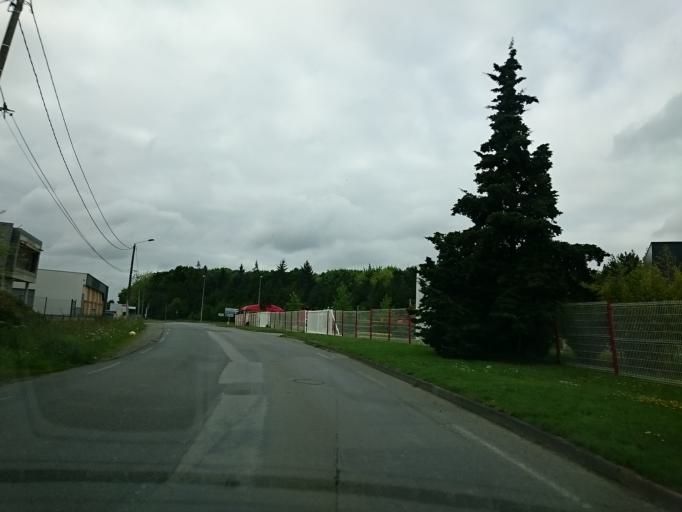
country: FR
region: Brittany
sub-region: Departement d'Ille-et-Vilaine
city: Vern-sur-Seiche
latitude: 48.0626
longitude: -1.6161
